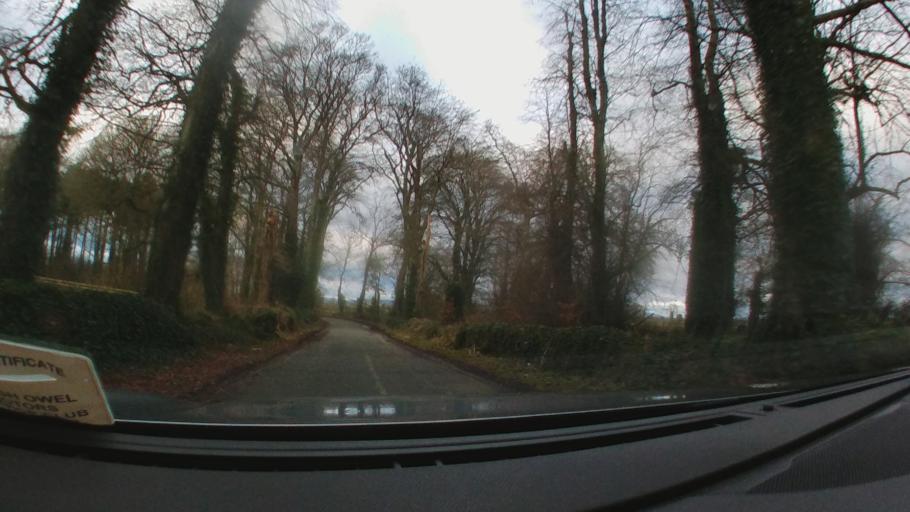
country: IE
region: Leinster
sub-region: Kilkenny
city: Thomastown
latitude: 52.5628
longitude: -7.1400
